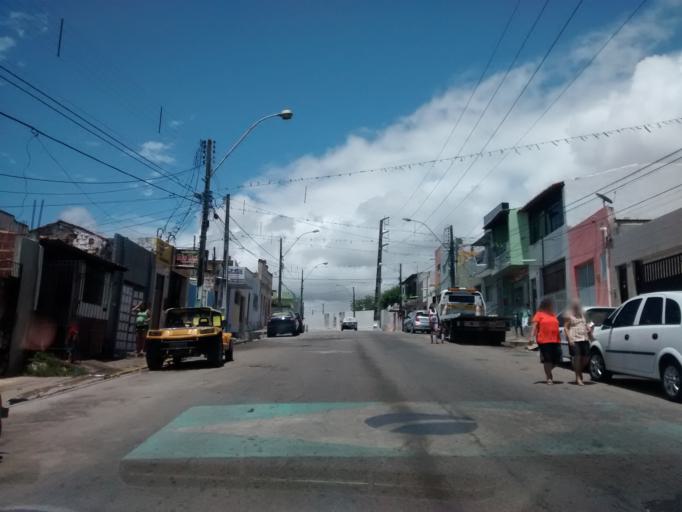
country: BR
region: Rio Grande do Norte
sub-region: Natal
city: Natal
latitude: -5.7912
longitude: -35.2133
